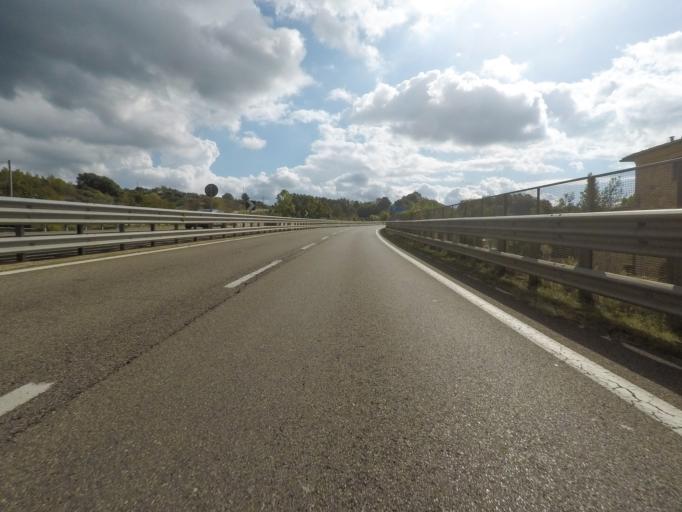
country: IT
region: Tuscany
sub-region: Provincia di Siena
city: Rapolano Terme
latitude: 43.3033
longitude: 11.5959
